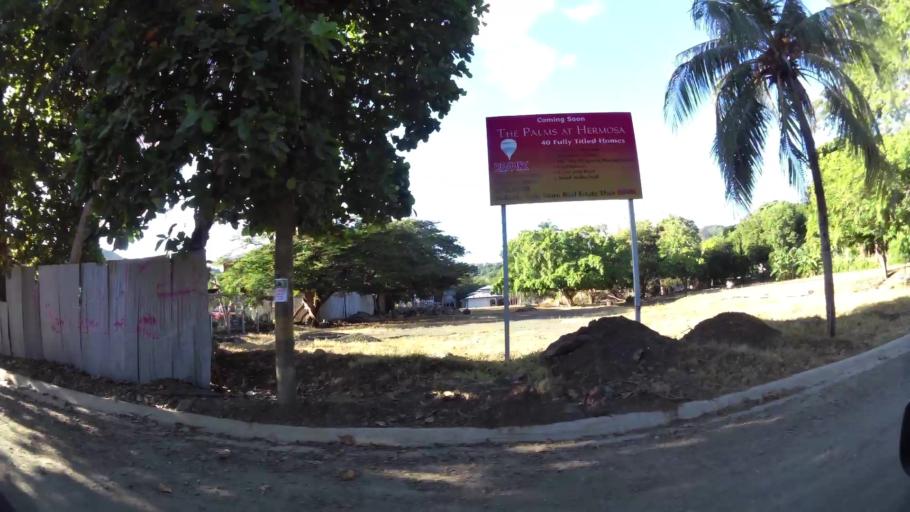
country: CR
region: Guanacaste
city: Sardinal
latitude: 10.5761
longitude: -85.6753
